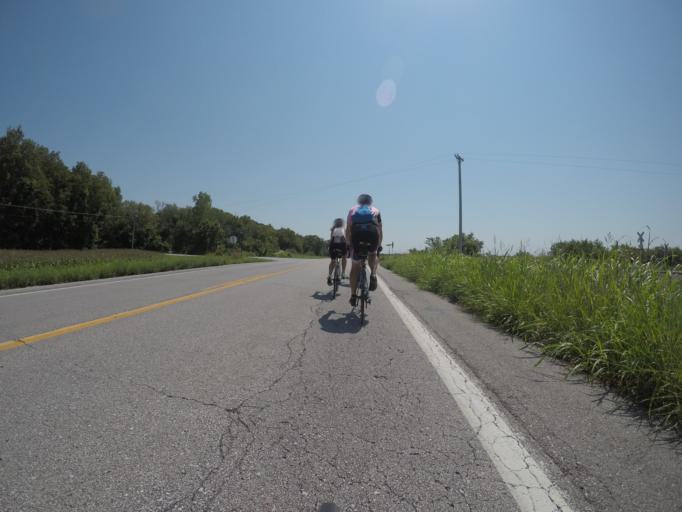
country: US
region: Kansas
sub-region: Leavenworth County
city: Leavenworth
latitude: 39.3282
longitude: -94.8573
